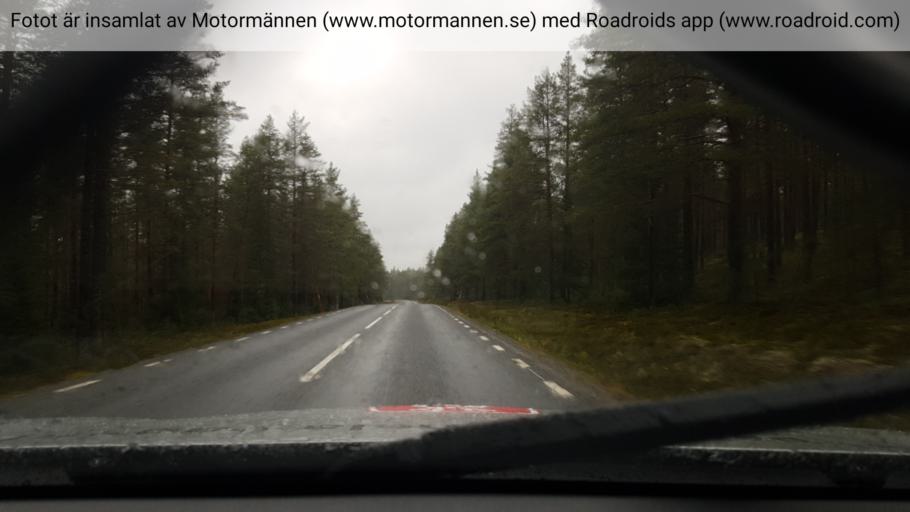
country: SE
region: Vaesterbotten
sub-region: Bjurholms Kommun
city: Bjurholm
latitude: 63.9679
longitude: 18.8402
